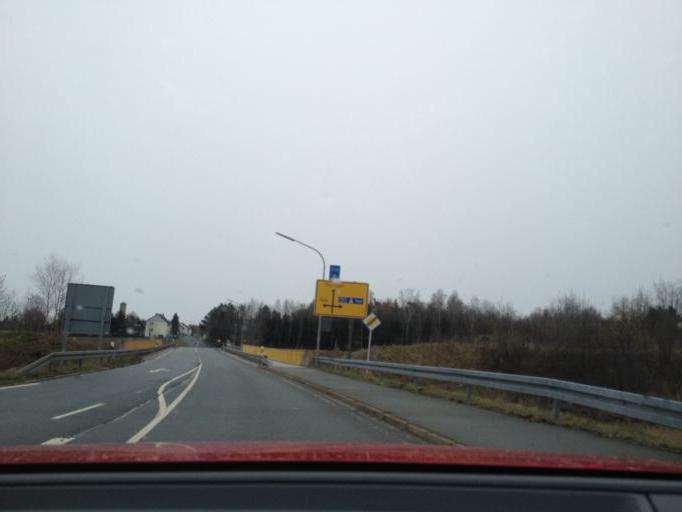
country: DE
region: Bavaria
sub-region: Upper Franconia
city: Hochstadt bei Thiersheim
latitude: 50.1028
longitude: 12.0936
